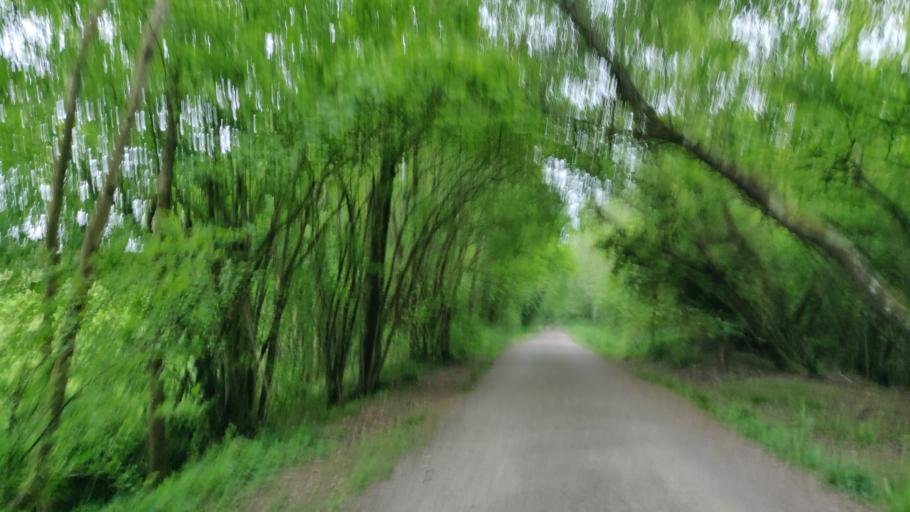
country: GB
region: England
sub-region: West Sussex
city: Southwater
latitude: 51.0074
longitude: -0.3279
